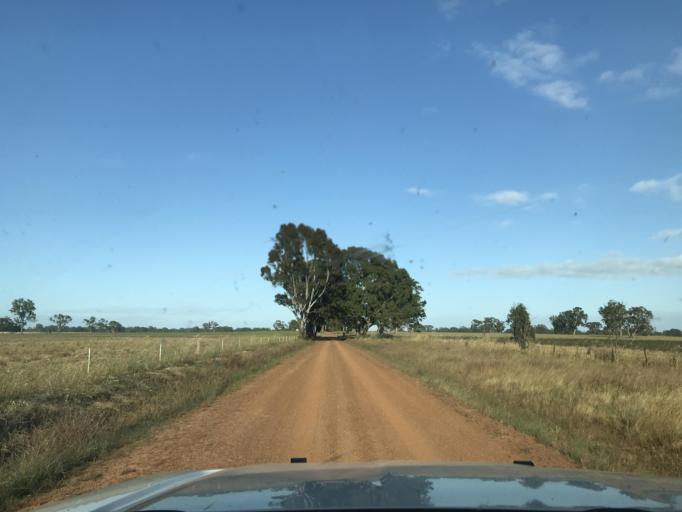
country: AU
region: South Australia
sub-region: Naracoorte and Lucindale
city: Naracoorte
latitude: -36.9567
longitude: 141.3772
